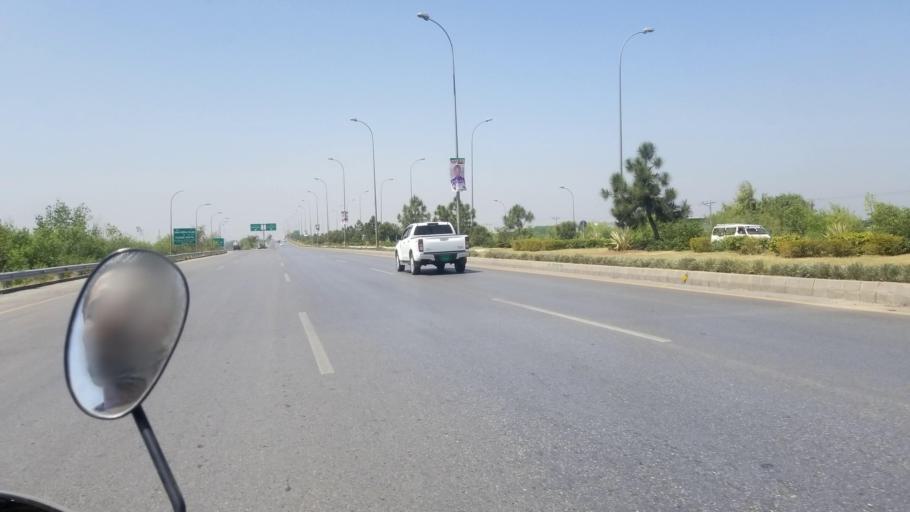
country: PK
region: Khyber Pakhtunkhwa
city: Peshawar
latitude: 34.0272
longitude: 71.6513
